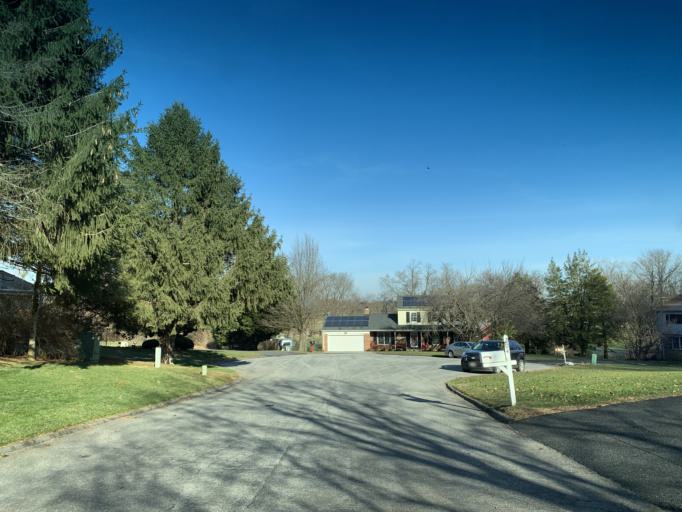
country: US
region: Maryland
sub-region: Harford County
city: South Bel Air
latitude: 39.5804
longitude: -76.2463
